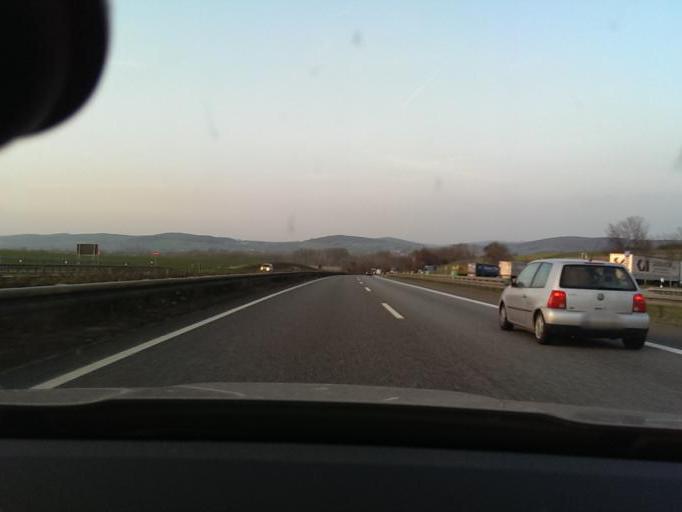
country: DE
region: Lower Saxony
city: Hillerse
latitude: 51.7159
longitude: 9.9416
